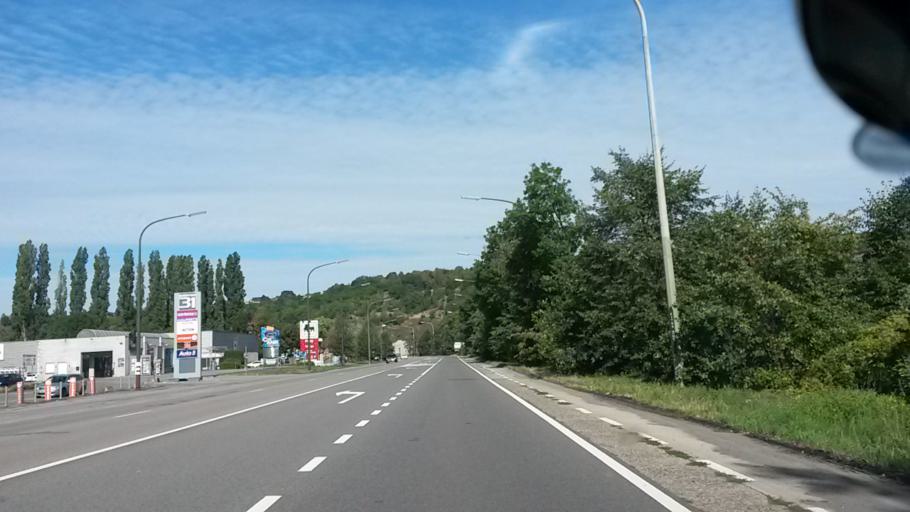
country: BE
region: Wallonia
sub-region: Province de Liege
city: Huy
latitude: 50.5329
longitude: 5.2637
